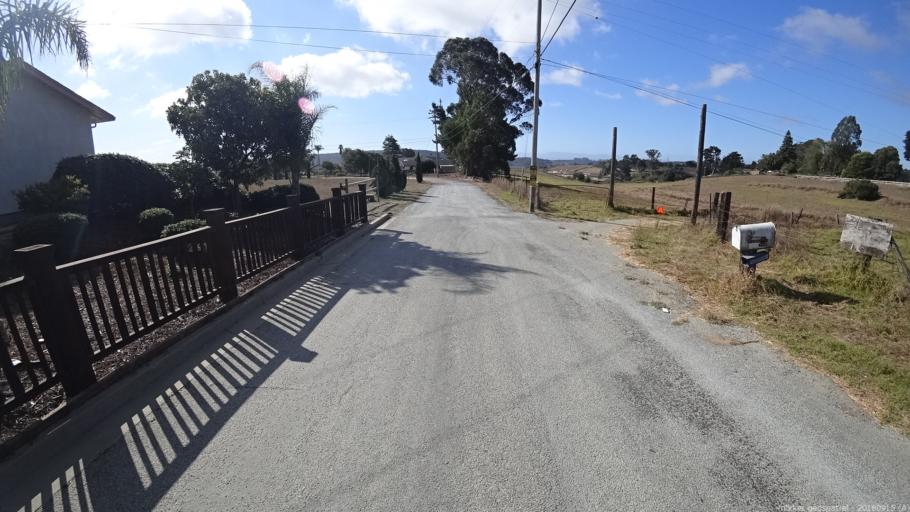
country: US
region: California
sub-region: Monterey County
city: Las Lomas
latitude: 36.8739
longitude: -121.7502
